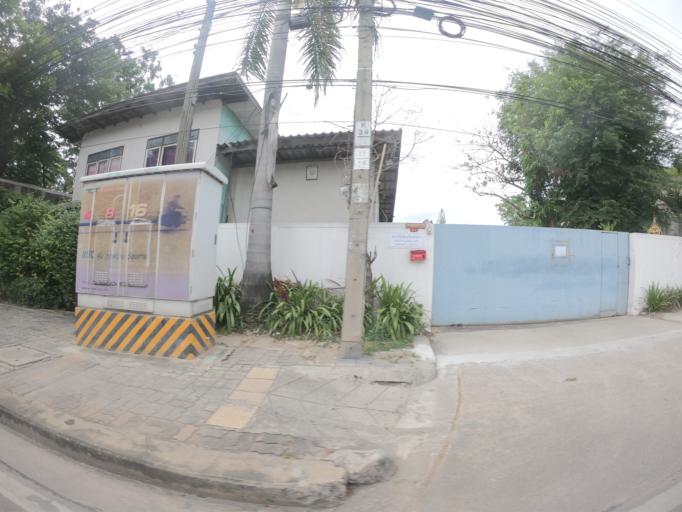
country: TH
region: Bangkok
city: Bang Na
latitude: 13.6776
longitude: 100.6517
